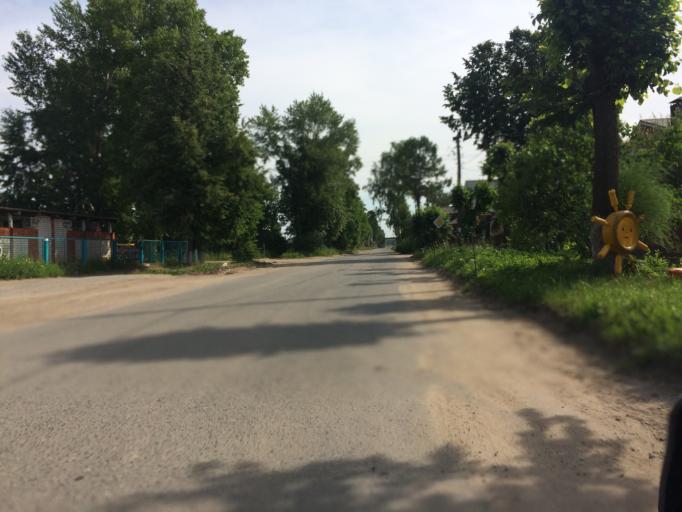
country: RU
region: Mariy-El
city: Yoshkar-Ola
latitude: 56.6483
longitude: 47.9096
